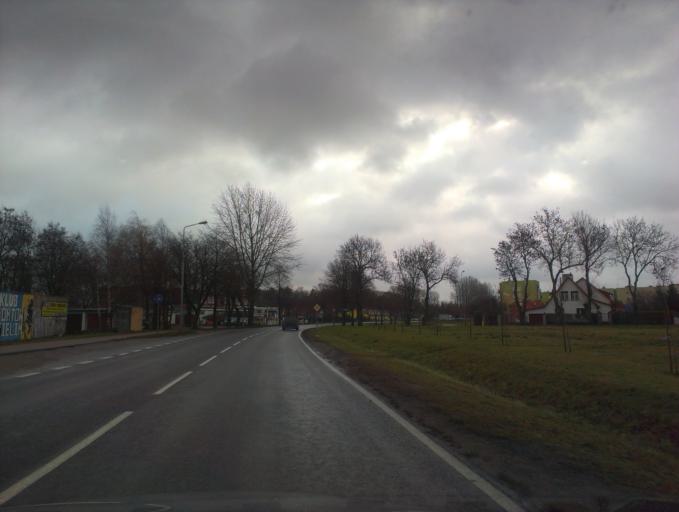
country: PL
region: West Pomeranian Voivodeship
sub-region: Powiat szczecinecki
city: Szczecinek
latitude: 53.7148
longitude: 16.6997
